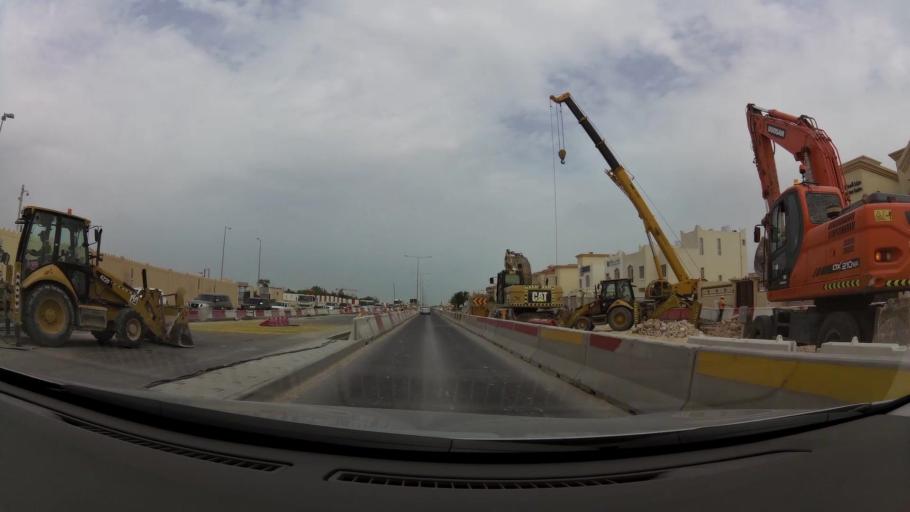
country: QA
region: Baladiyat ar Rayyan
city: Ar Rayyan
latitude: 25.3524
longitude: 51.4579
